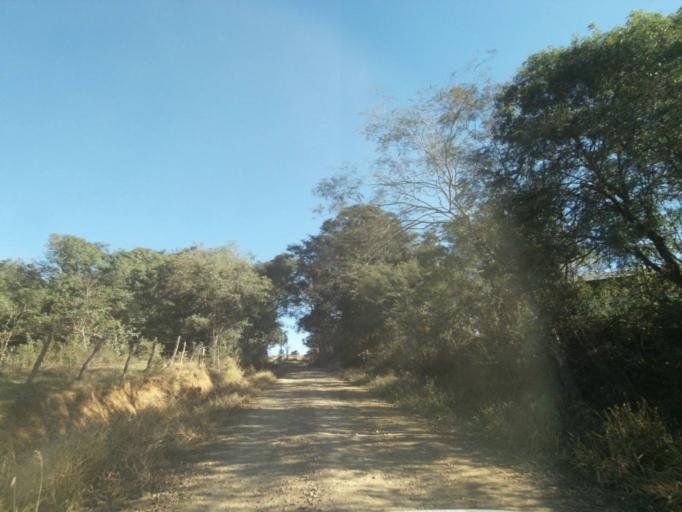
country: BR
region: Parana
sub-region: Tibagi
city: Tibagi
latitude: -24.5478
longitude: -50.5124
